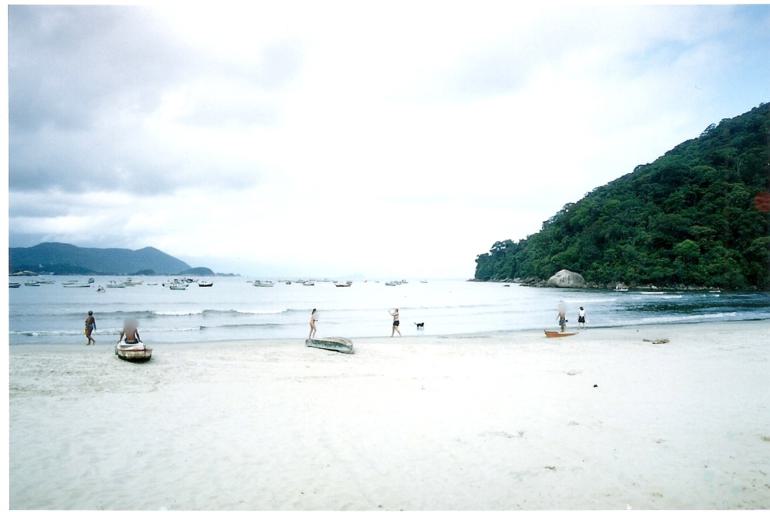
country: BR
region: Sao Paulo
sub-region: Bertioga
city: Bertioga
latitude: -23.9397
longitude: -46.1783
